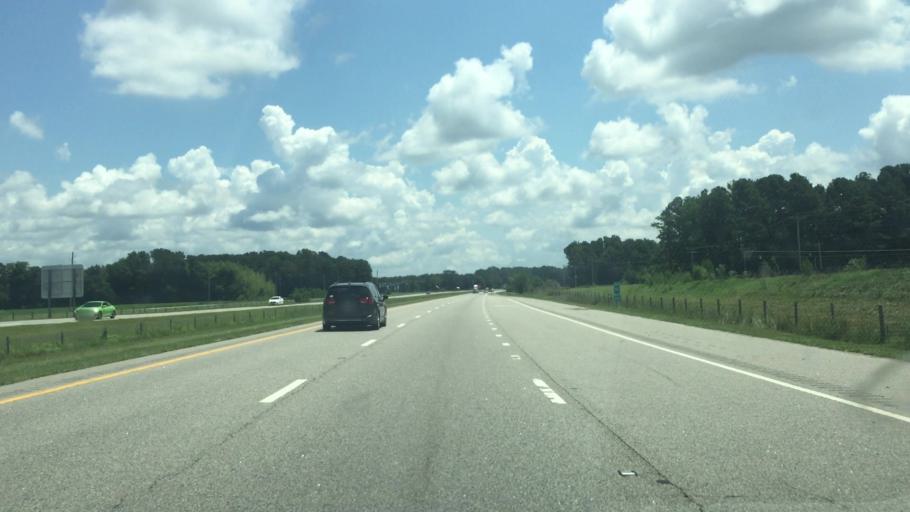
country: US
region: North Carolina
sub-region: Robeson County
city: Lumberton
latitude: 34.5935
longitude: -79.0821
